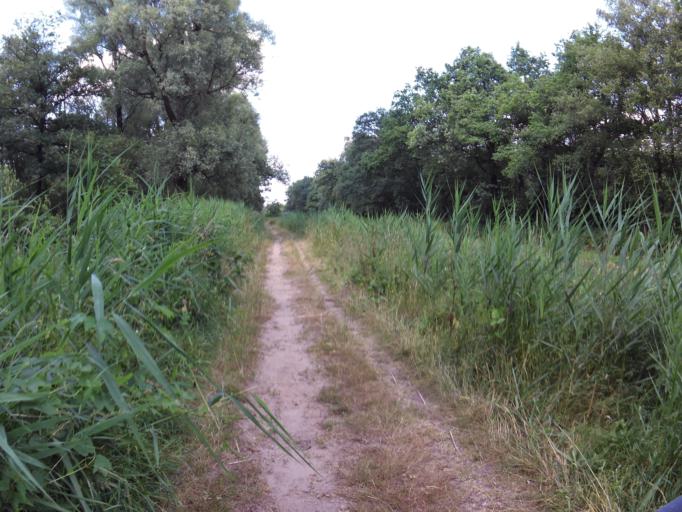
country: NL
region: North Brabant
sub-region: Gemeente Oirschot
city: Oirschot
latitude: 51.5479
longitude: 5.2707
